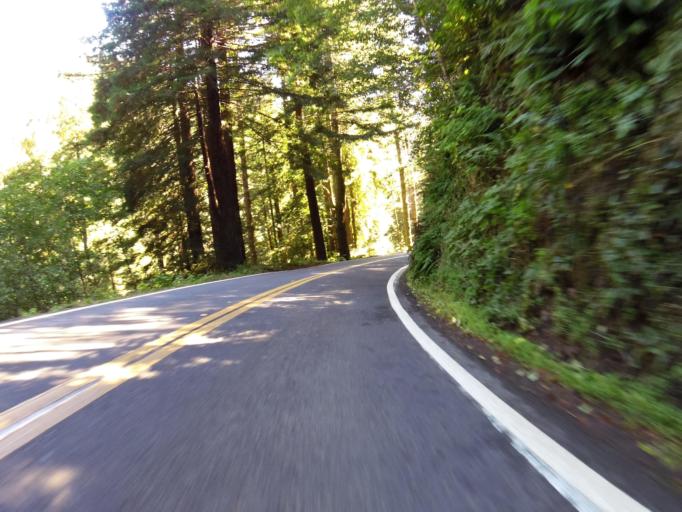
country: US
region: California
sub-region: Mendocino County
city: Fort Bragg
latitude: 39.7168
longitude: -123.8005
